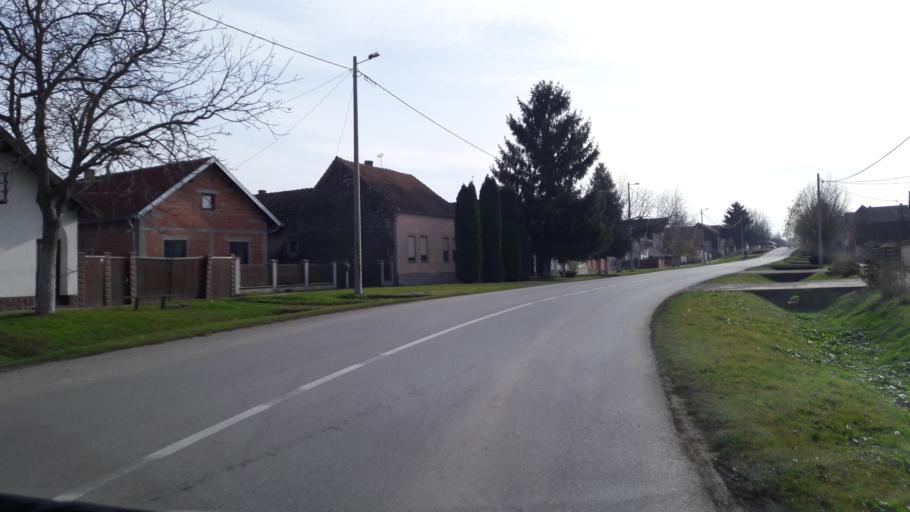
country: HR
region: Osjecko-Baranjska
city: Semeljci
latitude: 45.3563
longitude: 18.5535
